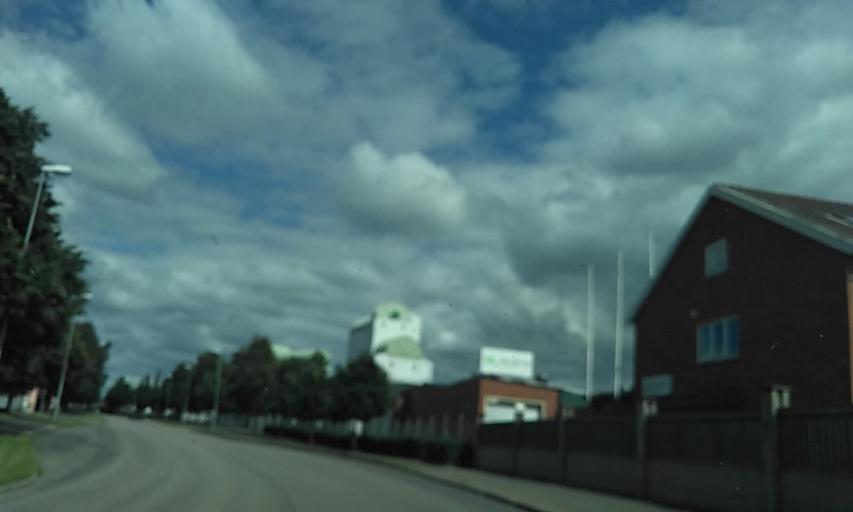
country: SE
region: Vaestra Goetaland
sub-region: Skara Kommun
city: Skara
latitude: 58.3843
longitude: 13.4470
